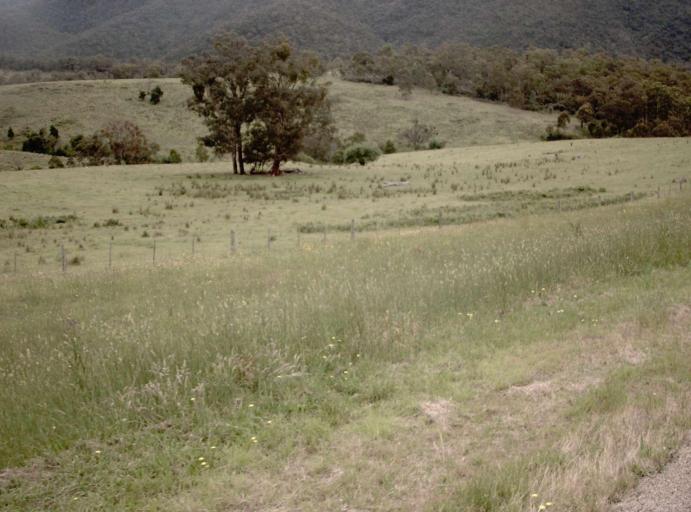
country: AU
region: Victoria
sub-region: East Gippsland
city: Bairnsdale
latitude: -37.5591
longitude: 147.1956
